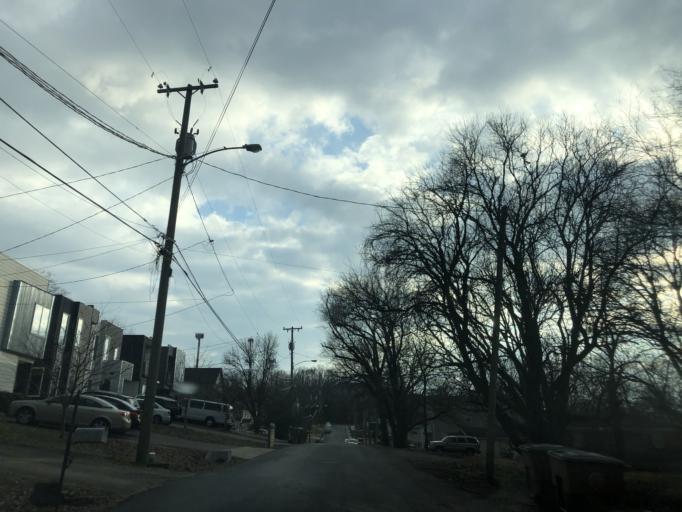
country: US
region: Tennessee
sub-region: Davidson County
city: Nashville
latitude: 36.1972
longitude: -86.7294
